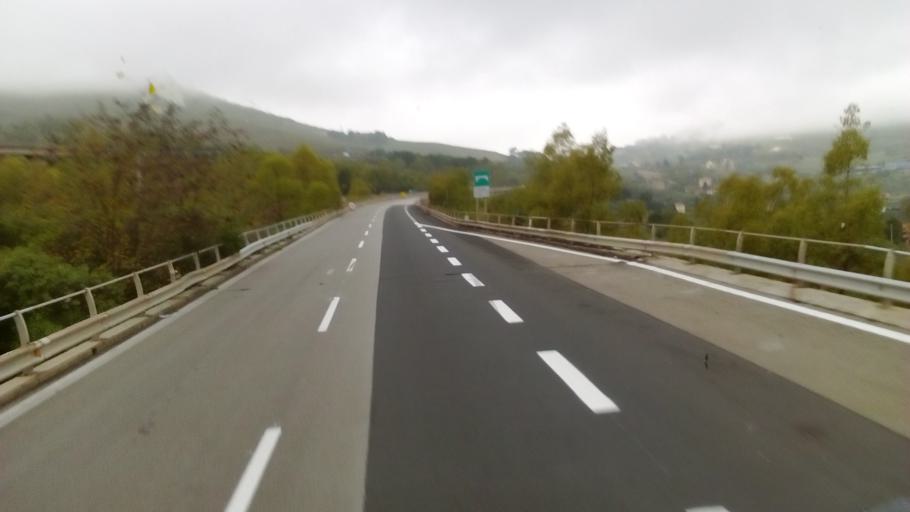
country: IT
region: Sicily
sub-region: Enna
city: Enna
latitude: 37.5788
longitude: 14.2978
